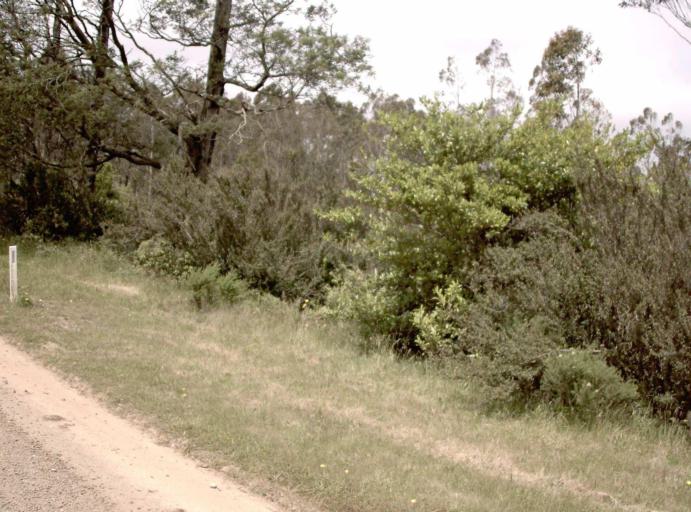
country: AU
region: Victoria
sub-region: Latrobe
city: Traralgon
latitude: -38.4181
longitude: 146.6115
